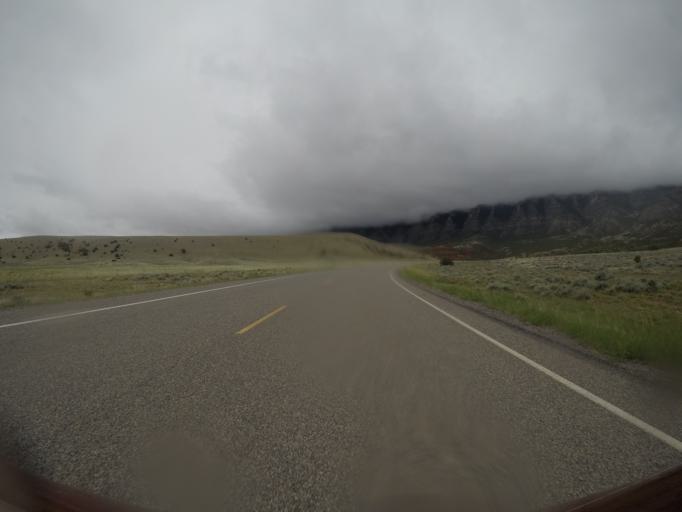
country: US
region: Wyoming
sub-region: Big Horn County
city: Lovell
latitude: 45.0849
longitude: -108.2524
